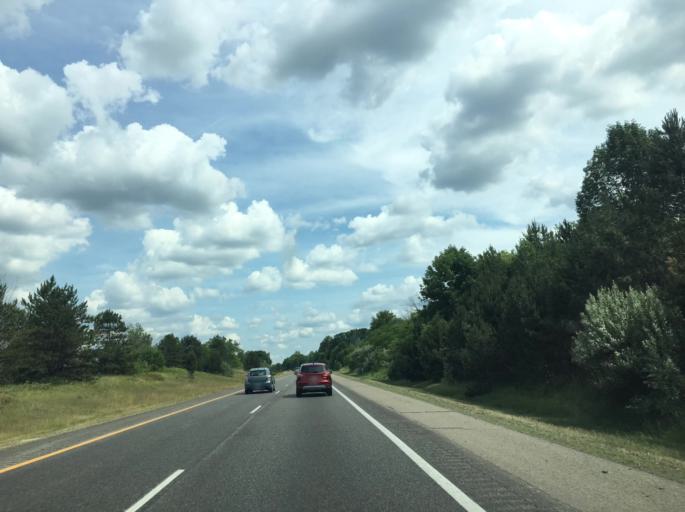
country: US
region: Michigan
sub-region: Genesee County
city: Grand Blanc
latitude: 42.9253
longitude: -83.6880
